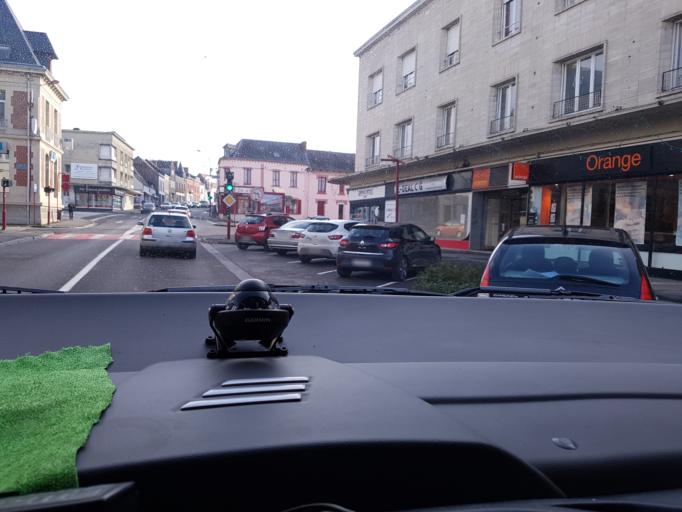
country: FR
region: Picardie
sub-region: Departement de l'Aisne
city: Hirson
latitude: 49.9234
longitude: 4.0818
